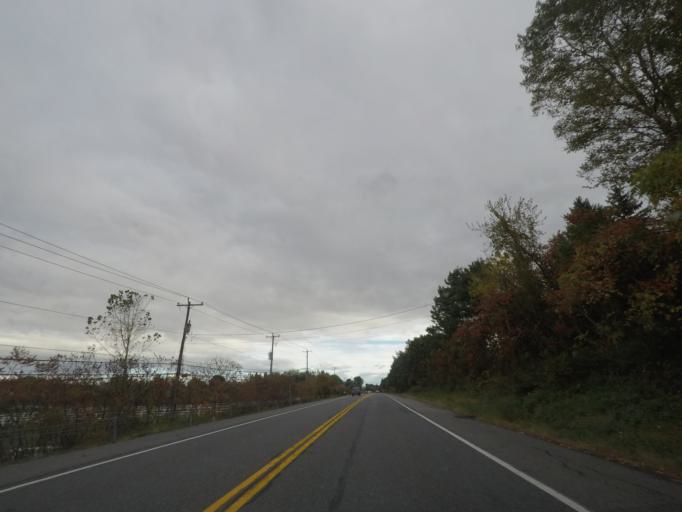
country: US
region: New York
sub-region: Saratoga County
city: Mechanicville
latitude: 42.8759
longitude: -73.7239
